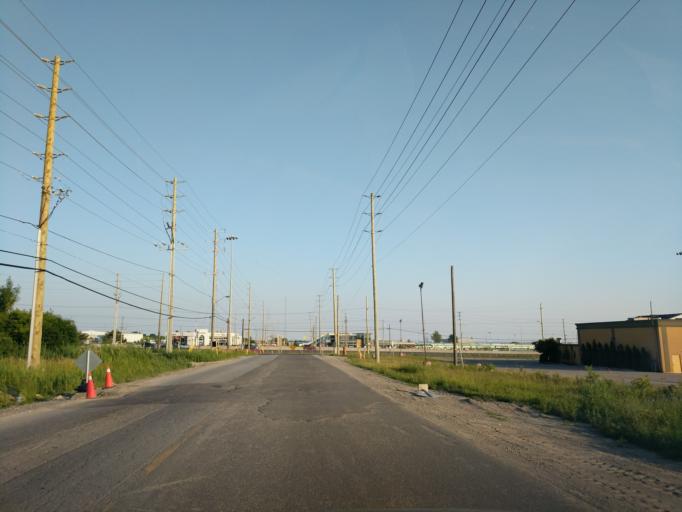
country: CA
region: Ontario
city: Oshawa
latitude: 43.8753
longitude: -78.8859
